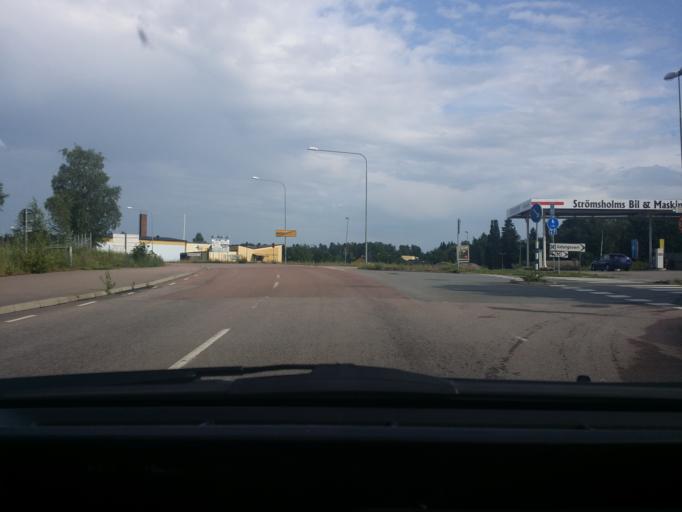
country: SE
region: Vaestmanland
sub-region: Hallstahammars Kommun
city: Kolback
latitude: 59.5648
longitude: 16.2387
